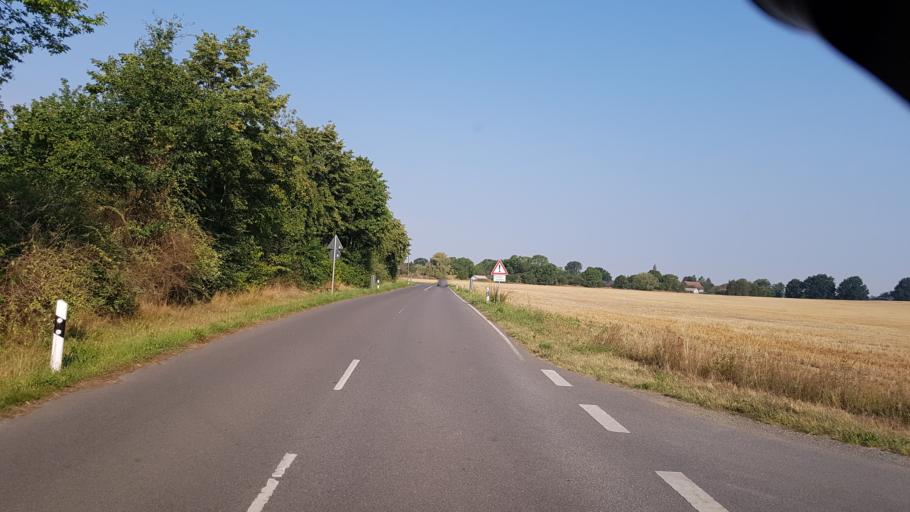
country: DE
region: Brandenburg
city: Drebkau
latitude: 51.6677
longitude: 14.2394
